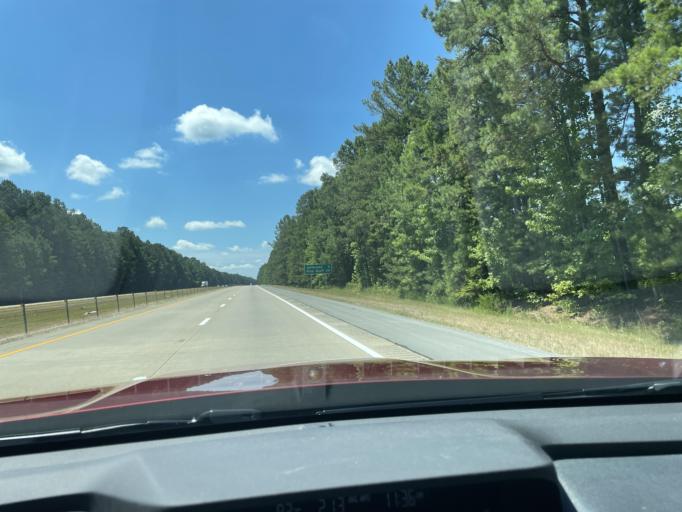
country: US
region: Arkansas
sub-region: Jefferson County
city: Redfield
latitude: 34.4293
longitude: -92.1935
